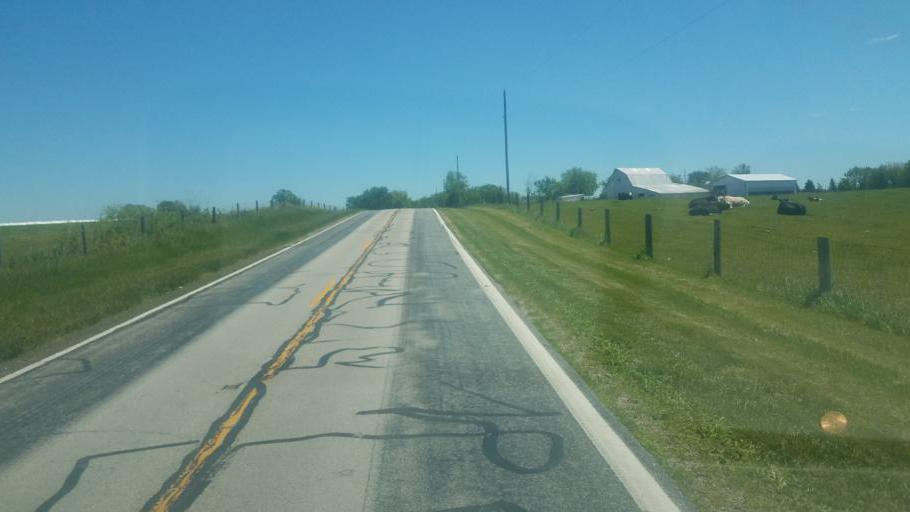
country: US
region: Ohio
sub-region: Darke County
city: Versailles
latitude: 40.2494
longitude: -84.5282
